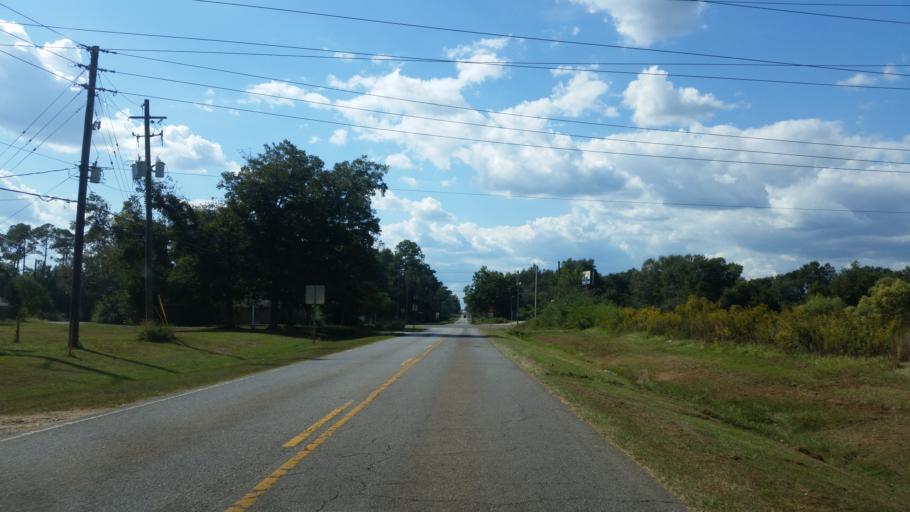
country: US
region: Florida
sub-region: Escambia County
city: Molino
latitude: 30.7169
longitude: -87.3481
